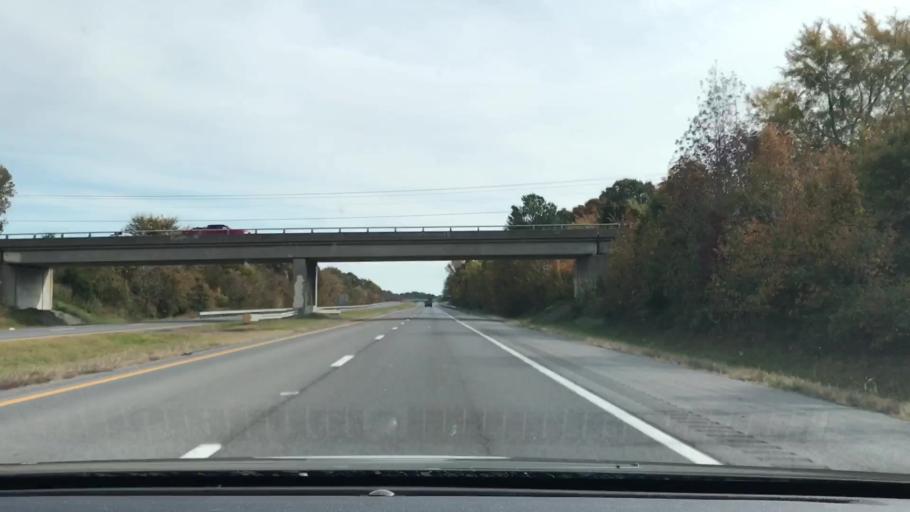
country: US
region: Kentucky
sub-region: Marshall County
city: Benton
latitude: 36.8473
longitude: -88.3935
